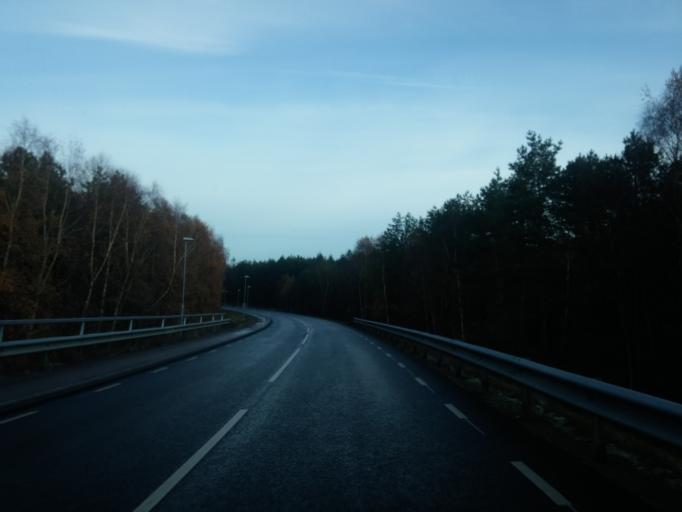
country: SE
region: Skane
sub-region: Angelholms Kommun
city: AEngelholm
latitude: 56.2157
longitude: 12.8042
